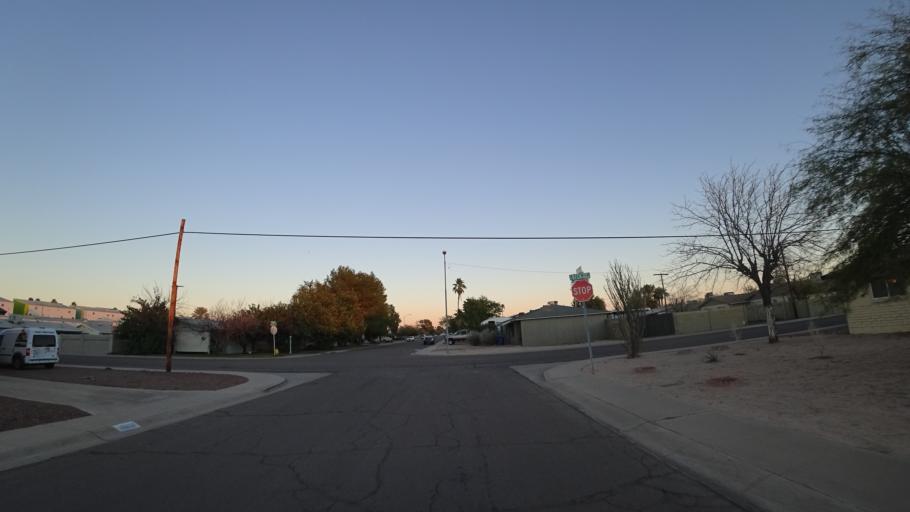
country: US
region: Arizona
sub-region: Maricopa County
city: Tempe Junction
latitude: 33.4203
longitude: -111.9568
